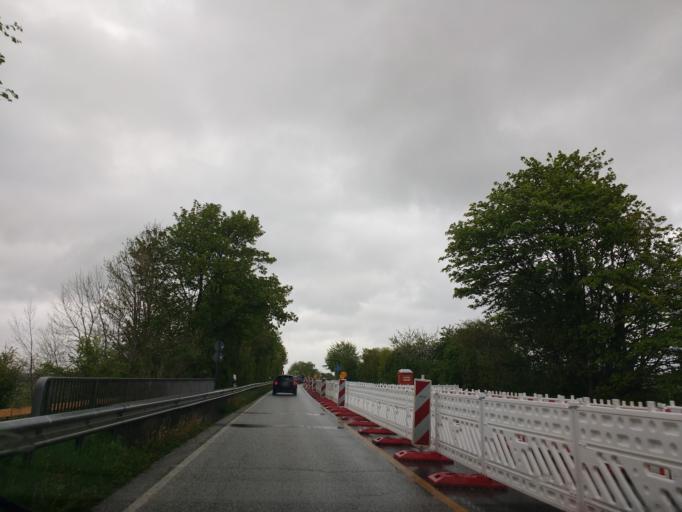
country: DE
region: Schleswig-Holstein
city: Barkelsby
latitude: 54.5034
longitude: 9.8527
